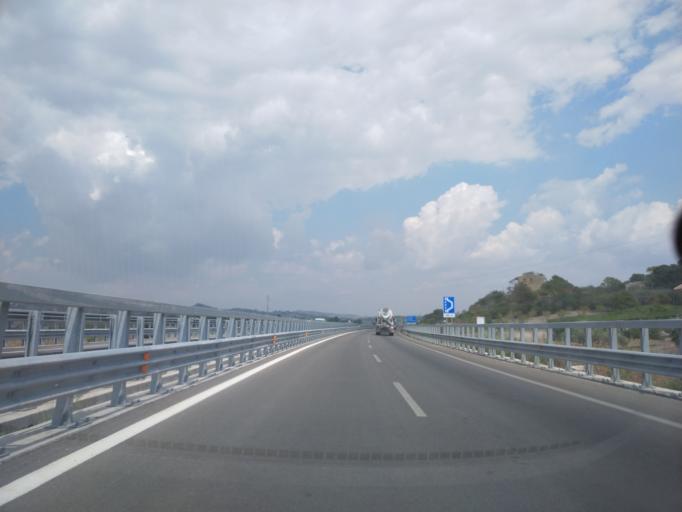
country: IT
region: Sicily
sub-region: Agrigento
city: Grotte
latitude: 37.3704
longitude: 13.7095
